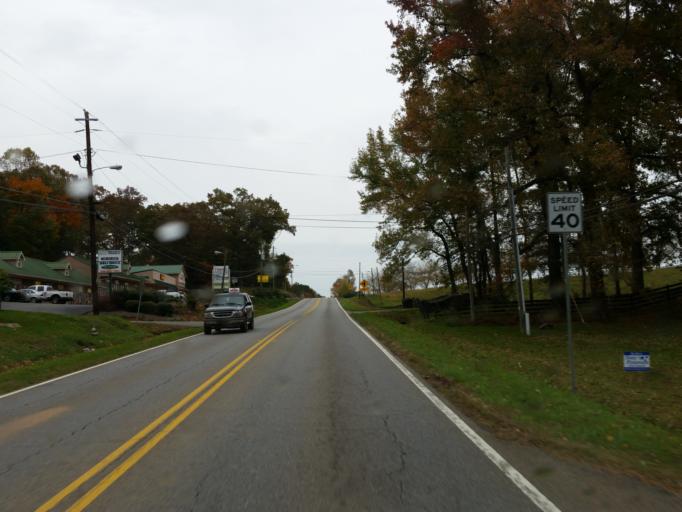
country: US
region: Georgia
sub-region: Pickens County
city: Jasper
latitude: 34.4658
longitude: -84.4425
